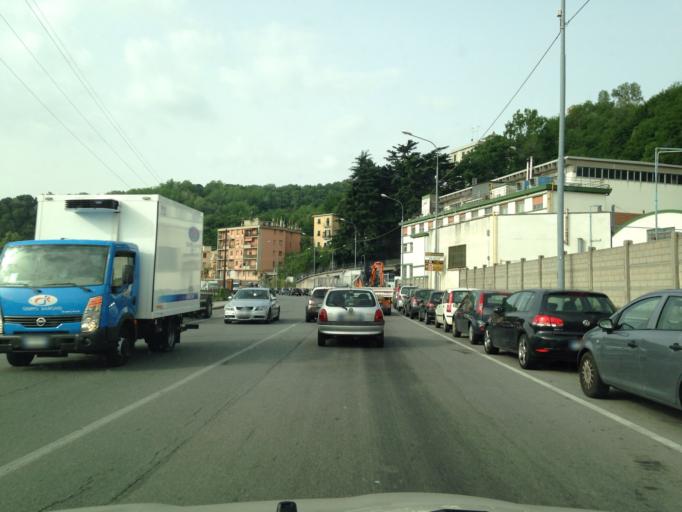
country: IT
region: Liguria
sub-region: Provincia di Genova
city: Manesseno
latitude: 44.4643
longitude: 8.8974
